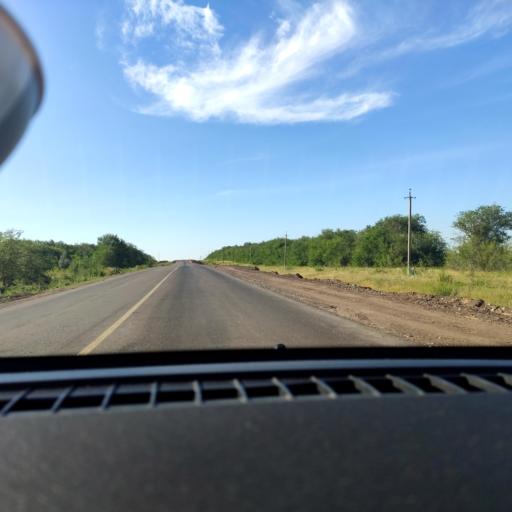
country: RU
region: Samara
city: Krasnoarmeyskoye
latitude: 52.8468
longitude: 49.9989
